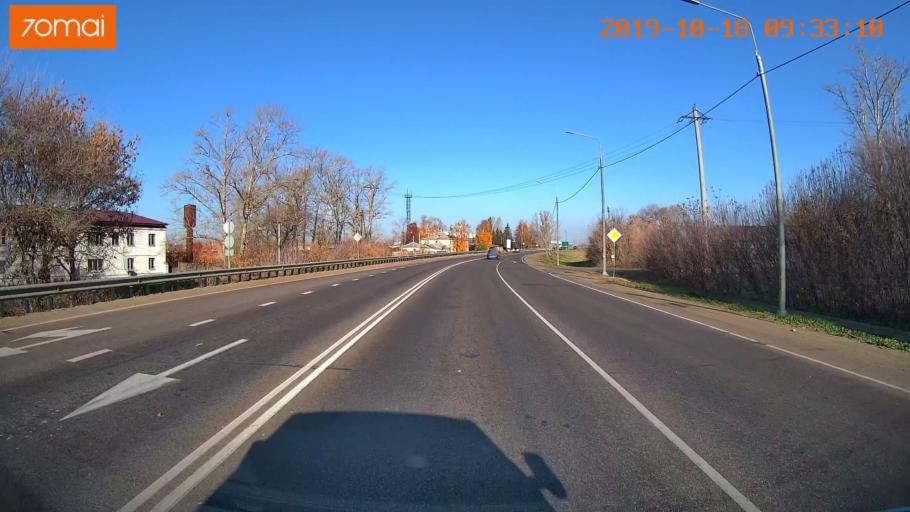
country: RU
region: Tula
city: Yefremov
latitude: 53.1638
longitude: 38.1524
